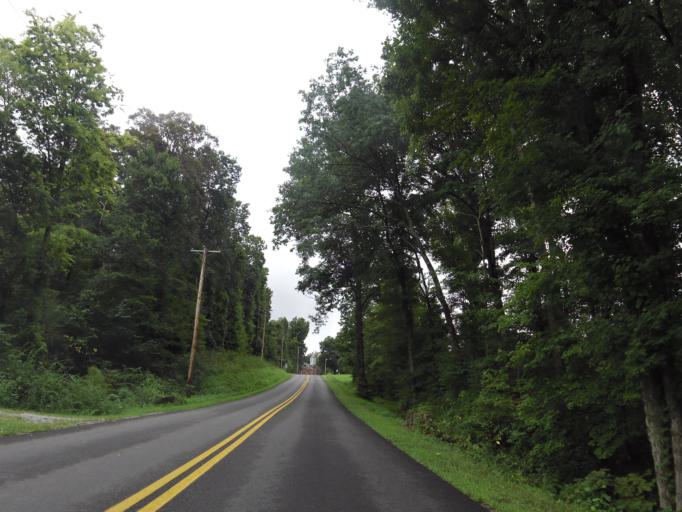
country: US
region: Missouri
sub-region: Cape Girardeau County
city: Cape Girardeau
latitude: 37.3546
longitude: -89.5624
